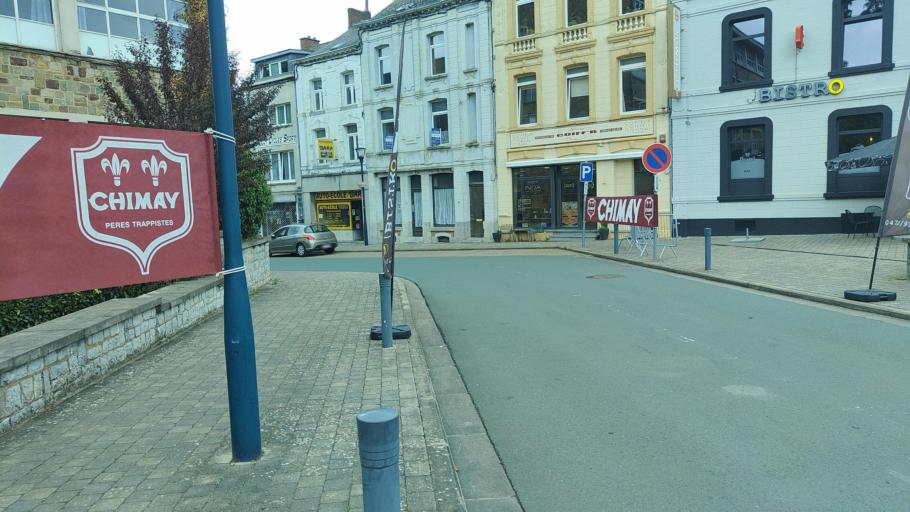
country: BE
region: Wallonia
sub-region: Province du Hainaut
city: Chimay
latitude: 50.0488
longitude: 4.3194
